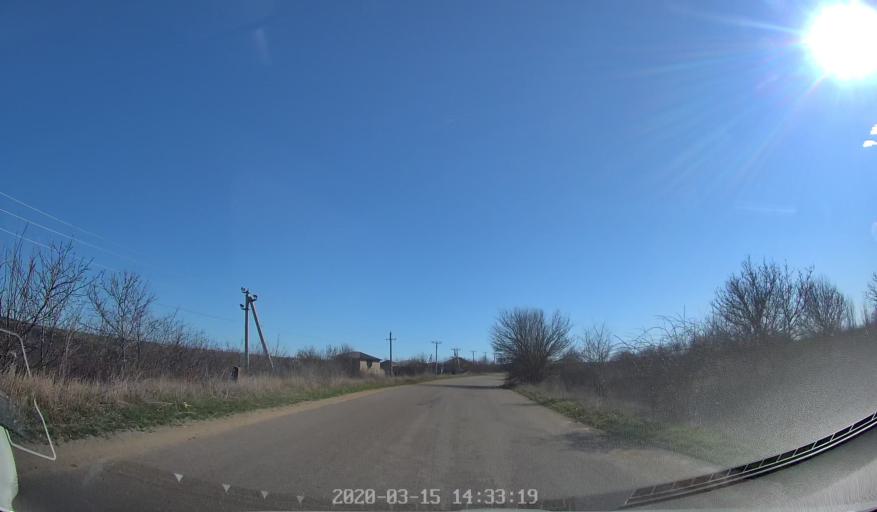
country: MD
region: Orhei
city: Orhei
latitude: 47.3385
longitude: 28.9168
